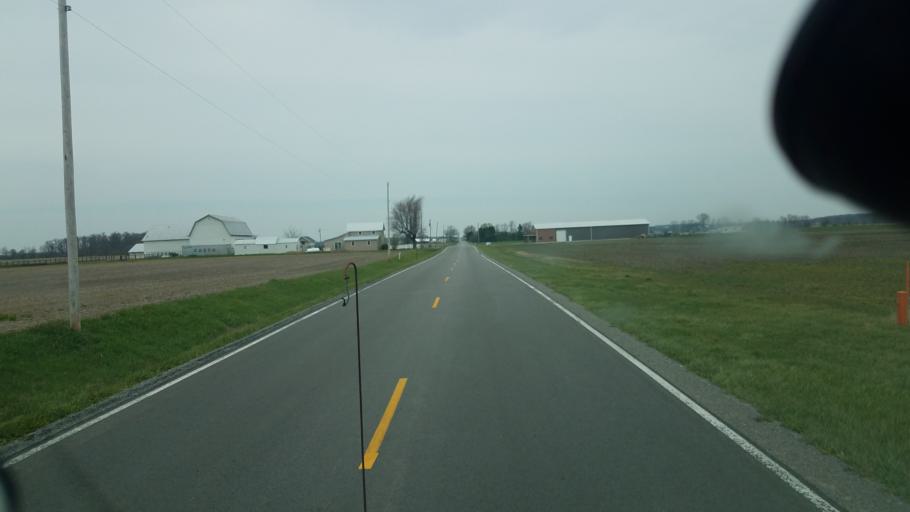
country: US
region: Ohio
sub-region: Wyandot County
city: Carey
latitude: 41.0071
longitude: -83.4777
